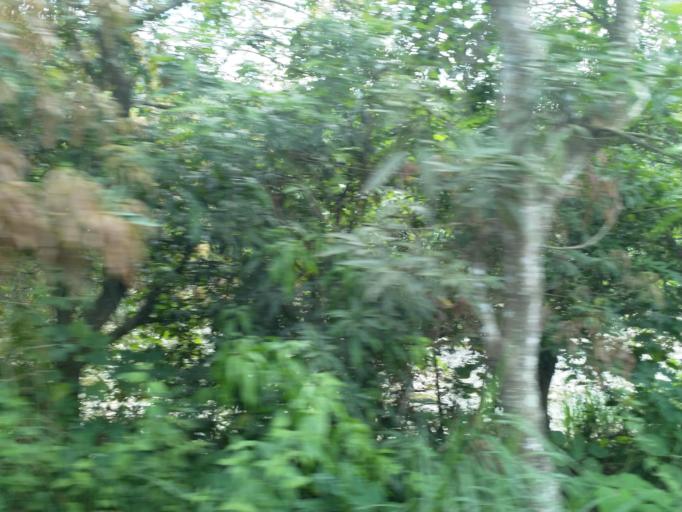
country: TW
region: Taiwan
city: Yujing
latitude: 22.9287
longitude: 120.5865
